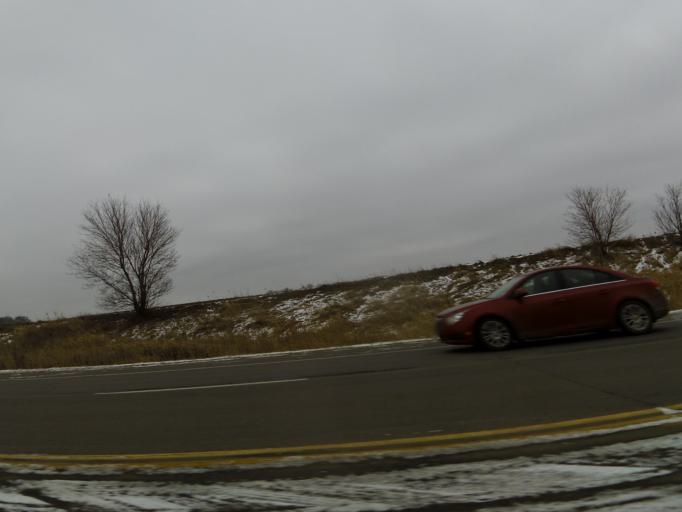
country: US
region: Minnesota
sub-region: Wright County
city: Montrose
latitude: 45.0649
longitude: -93.8543
